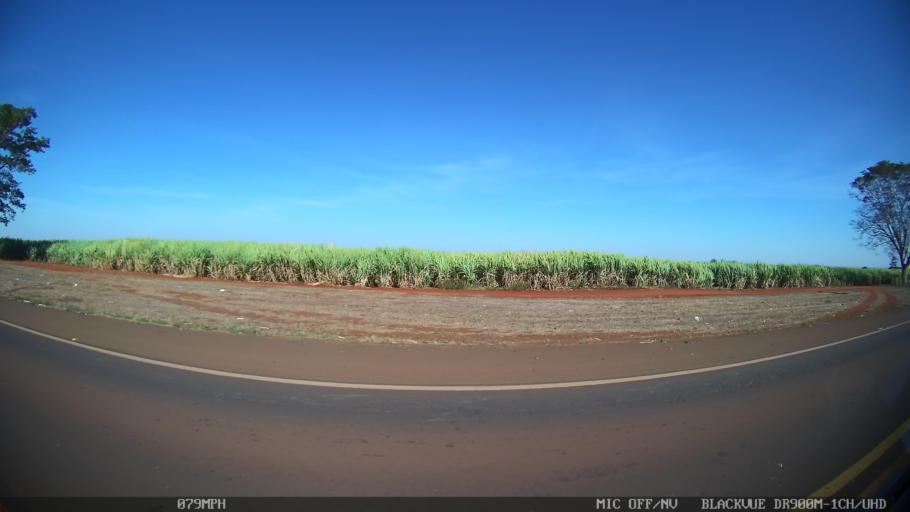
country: BR
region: Sao Paulo
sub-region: Guaira
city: Guaira
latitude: -20.4443
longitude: -48.2820
